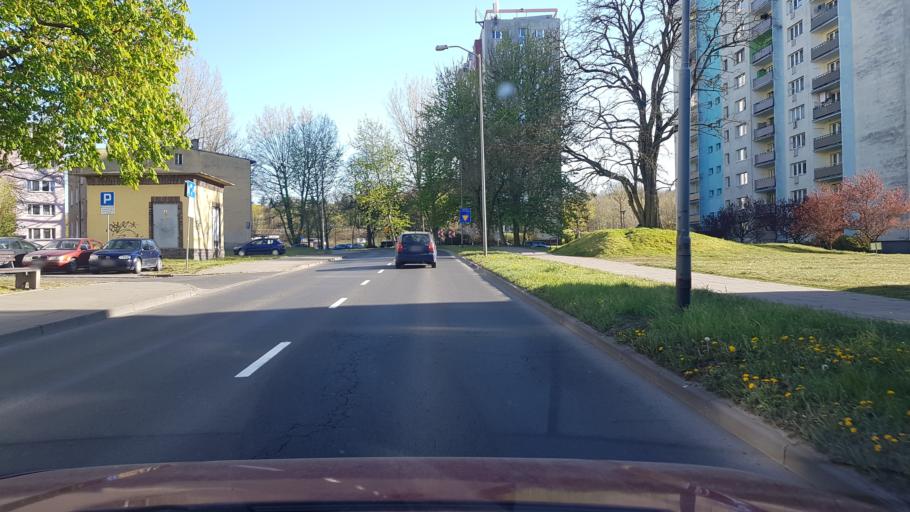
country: PL
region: West Pomeranian Voivodeship
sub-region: Szczecin
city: Szczecin
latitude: 53.3808
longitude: 14.6355
